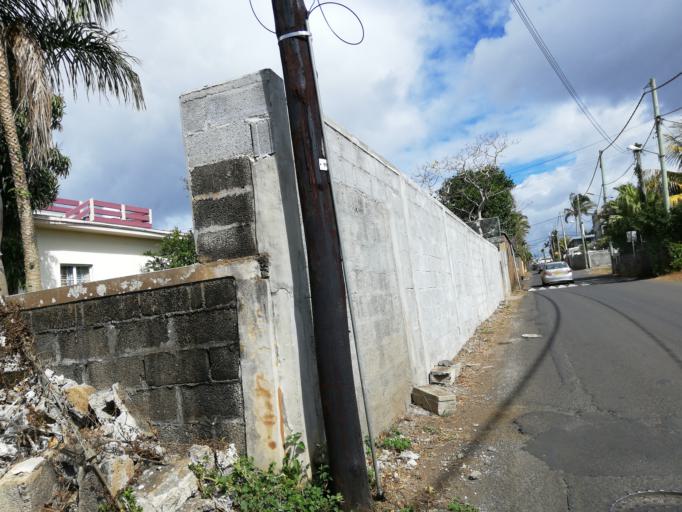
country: MU
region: Moka
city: Moka
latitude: -20.2199
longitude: 57.4755
